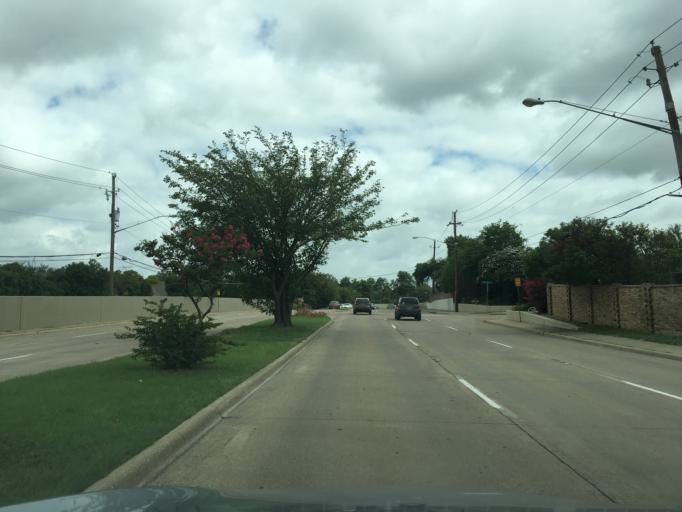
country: US
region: Texas
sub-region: Dallas County
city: Richardson
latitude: 32.8897
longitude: -96.7416
